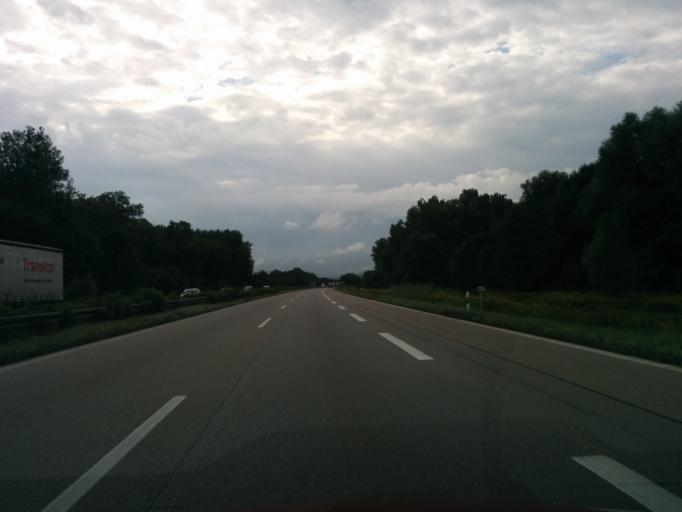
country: DE
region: Bavaria
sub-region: Lower Bavaria
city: Niederalteich
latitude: 48.7871
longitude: 13.0128
